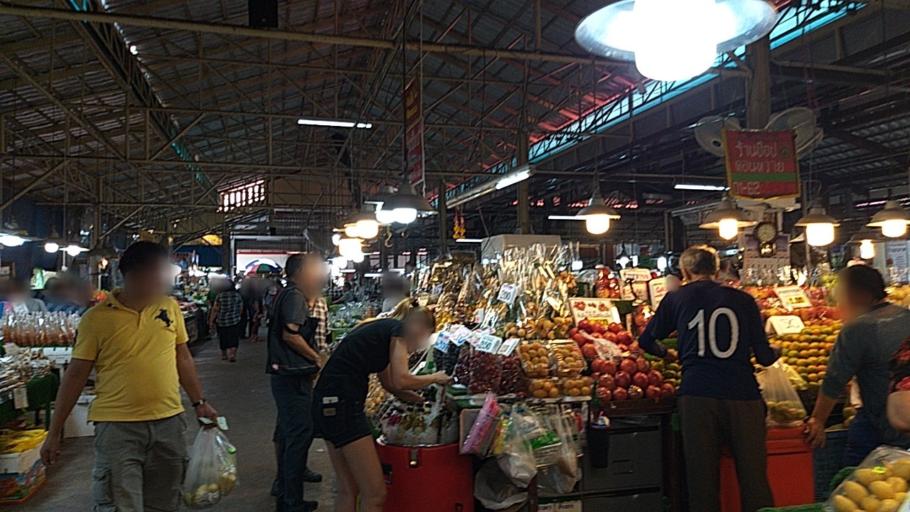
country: TH
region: Nakhon Pathom
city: Salaya
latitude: 13.7709
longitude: 100.2839
